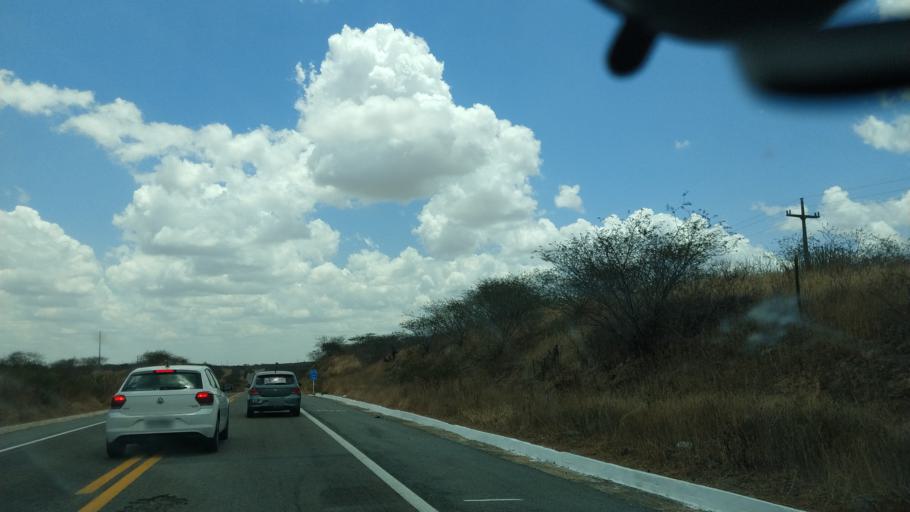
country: BR
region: Rio Grande do Norte
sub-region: Cerro Cora
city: Cerro Cora
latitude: -6.2008
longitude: -36.2727
